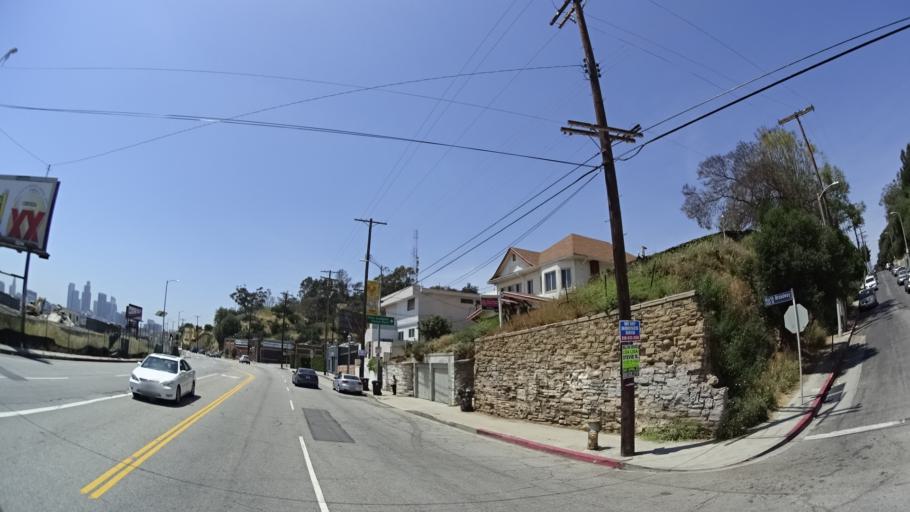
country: US
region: California
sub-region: Los Angeles County
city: Los Angeles
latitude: 34.0713
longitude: -118.2293
